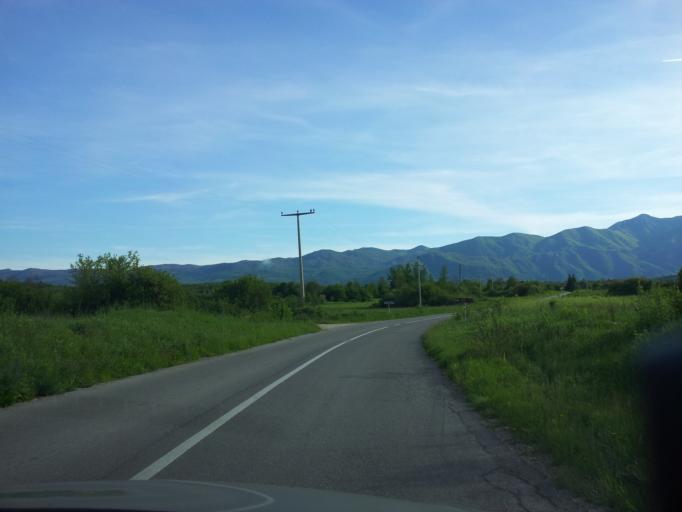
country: HR
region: Zadarska
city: Obrovac
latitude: 44.3769
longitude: 15.6729
